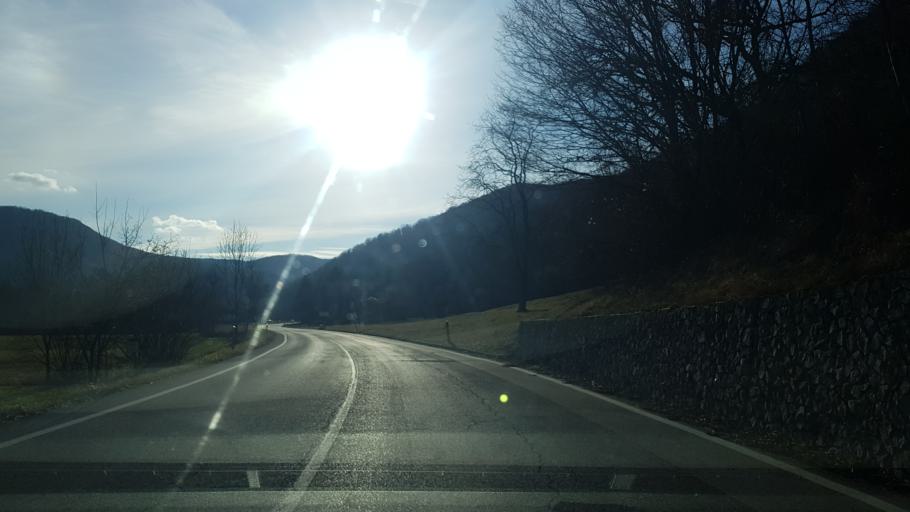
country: IT
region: Friuli Venezia Giulia
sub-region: Provincia di Udine
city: Merso di Sopra
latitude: 46.1303
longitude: 13.5305
